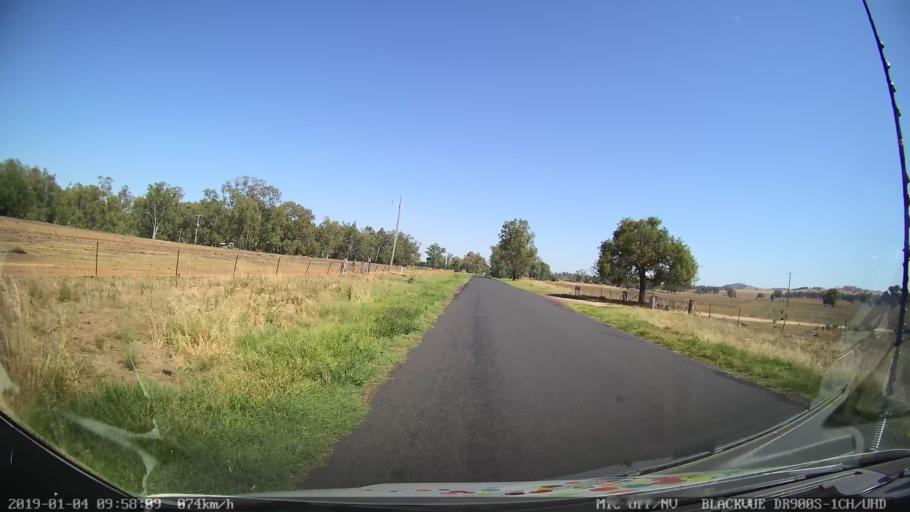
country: AU
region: New South Wales
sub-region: Cabonne
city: Canowindra
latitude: -33.5212
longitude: 148.3965
